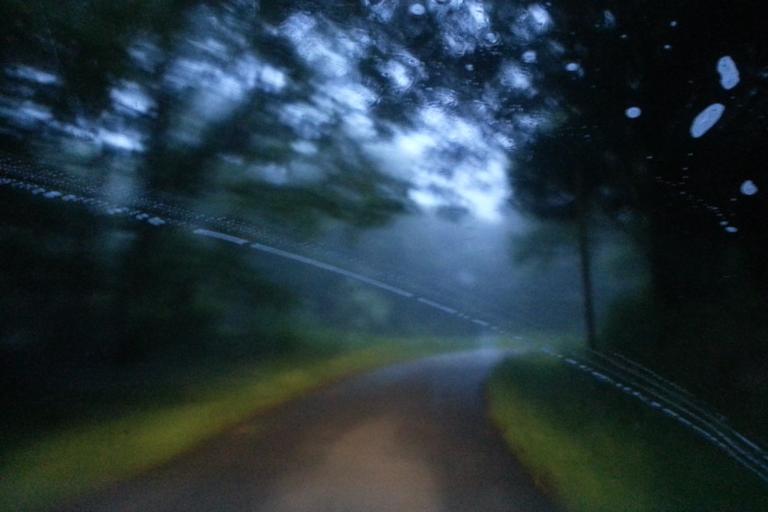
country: FR
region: Brittany
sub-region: Departement du Morbihan
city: Langonnet
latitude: 48.0813
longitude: -3.4600
